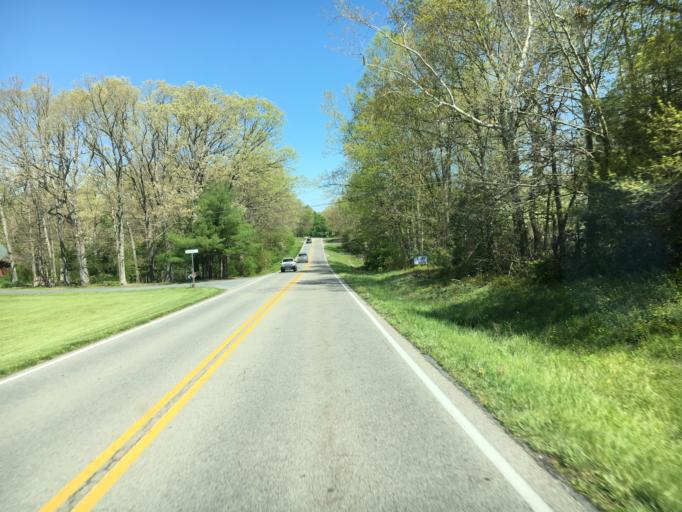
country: US
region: Virginia
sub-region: Augusta County
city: Crimora
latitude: 38.1615
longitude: -78.8489
